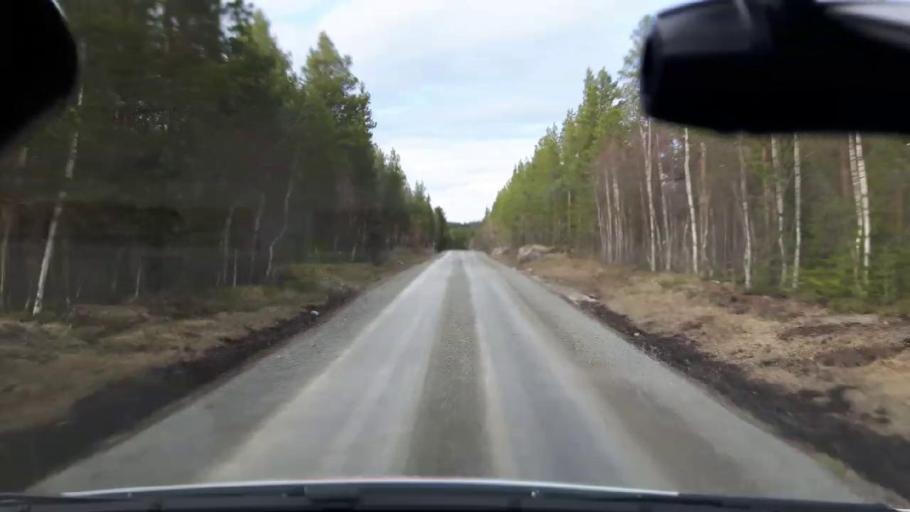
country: SE
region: Jaemtland
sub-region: Bergs Kommun
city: Hoverberg
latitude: 62.9289
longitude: 14.6467
